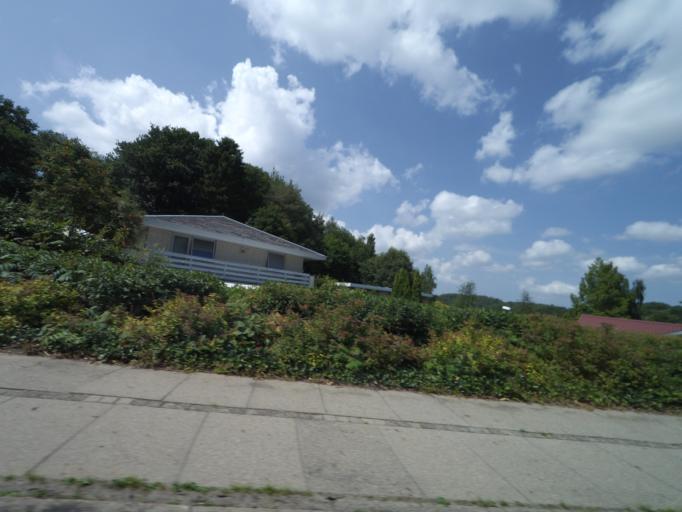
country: DK
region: South Denmark
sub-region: Assens Kommune
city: Arup
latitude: 55.3726
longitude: 10.0401
